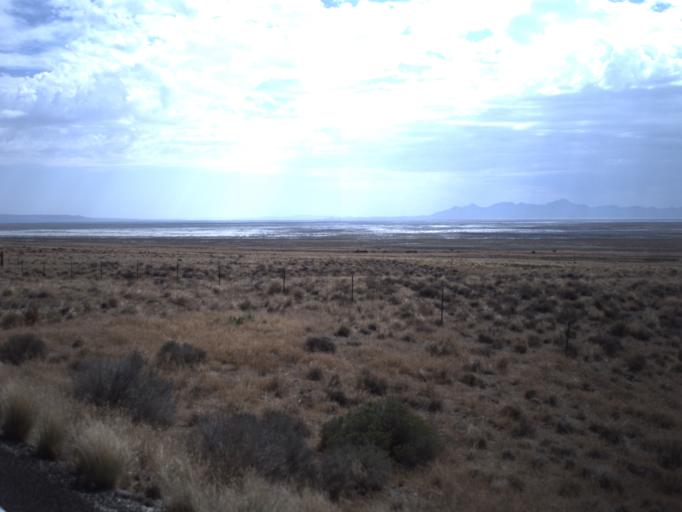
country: US
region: Utah
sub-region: Tooele County
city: Wendover
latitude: 41.4388
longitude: -113.7244
